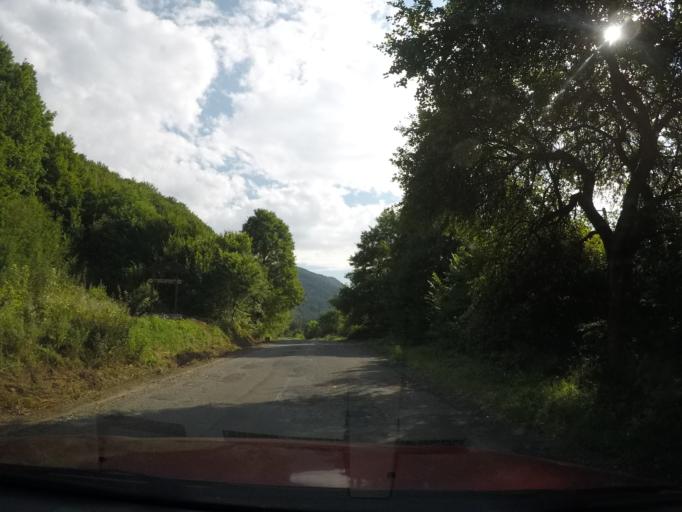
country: UA
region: Zakarpattia
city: Velykyi Bereznyi
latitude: 48.9365
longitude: 22.4660
